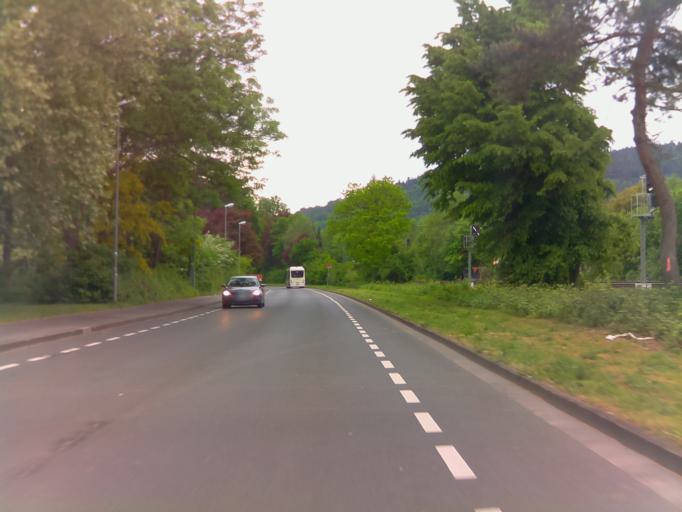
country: DE
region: Hesse
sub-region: Regierungsbezirk Giessen
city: Marburg an der Lahn
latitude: 50.8102
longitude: 8.7811
